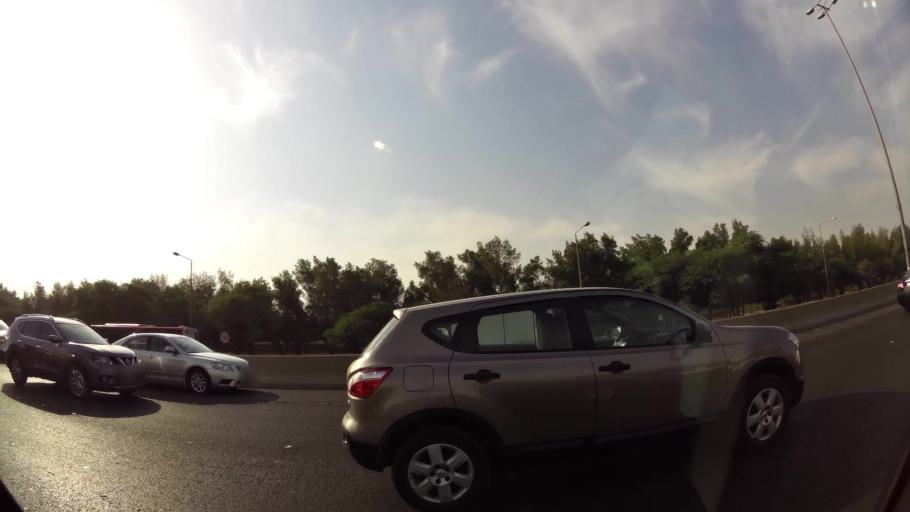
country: KW
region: Mubarak al Kabir
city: Sabah as Salim
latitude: 29.2645
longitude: 48.0595
